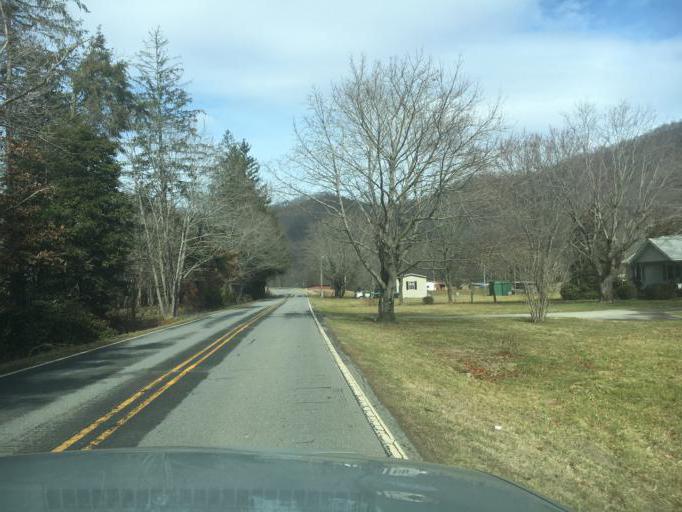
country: US
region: North Carolina
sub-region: Haywood County
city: Canton
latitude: 35.4538
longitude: -82.8413
